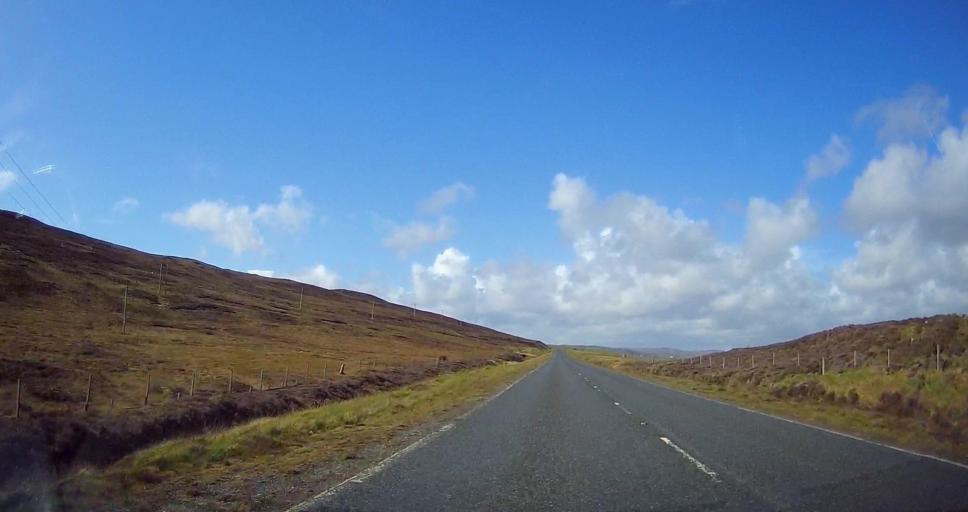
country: GB
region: Scotland
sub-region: Shetland Islands
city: Lerwick
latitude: 60.2107
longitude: -1.2336
